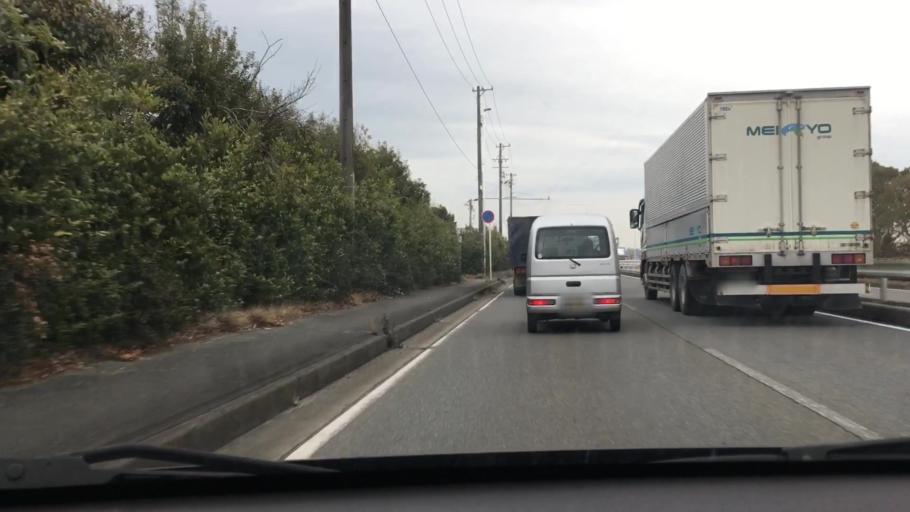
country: JP
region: Mie
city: Suzuka
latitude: 34.8837
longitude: 136.5265
